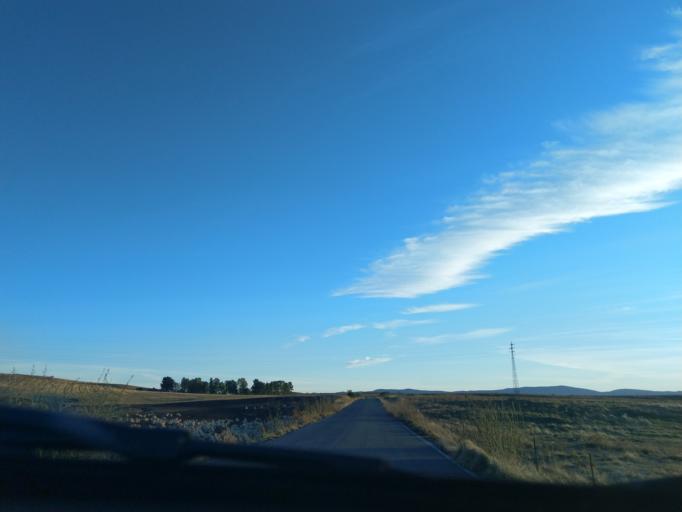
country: ES
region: Extremadura
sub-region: Provincia de Badajoz
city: Berlanga
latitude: 38.2606
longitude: -5.8261
